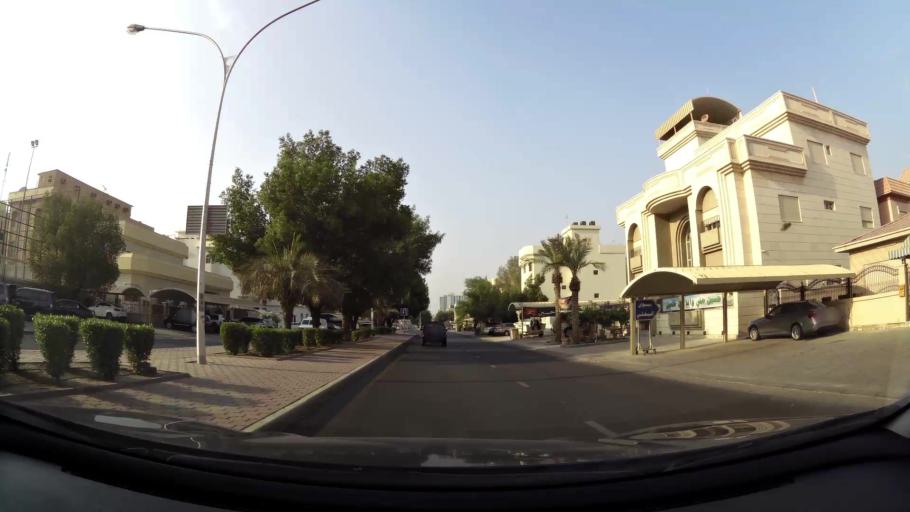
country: KW
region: Muhafazat Hawalli
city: Hawalli
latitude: 29.3186
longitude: 48.0333
